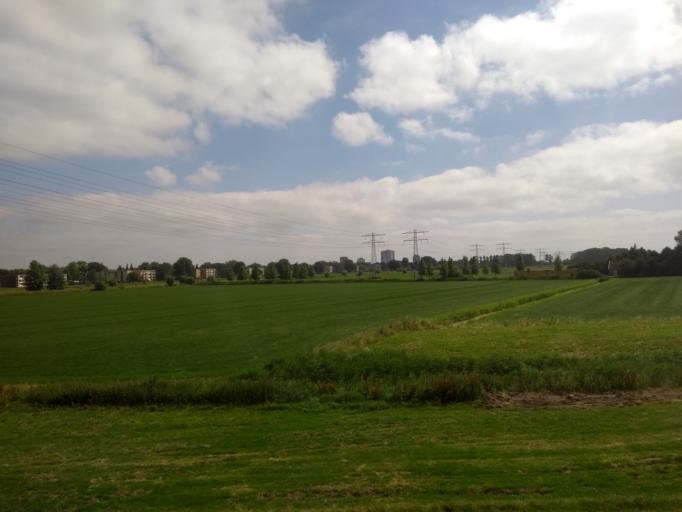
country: NL
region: Friesland
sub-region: Gemeente Leeuwarden
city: Goutum
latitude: 53.1818
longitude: 5.7762
